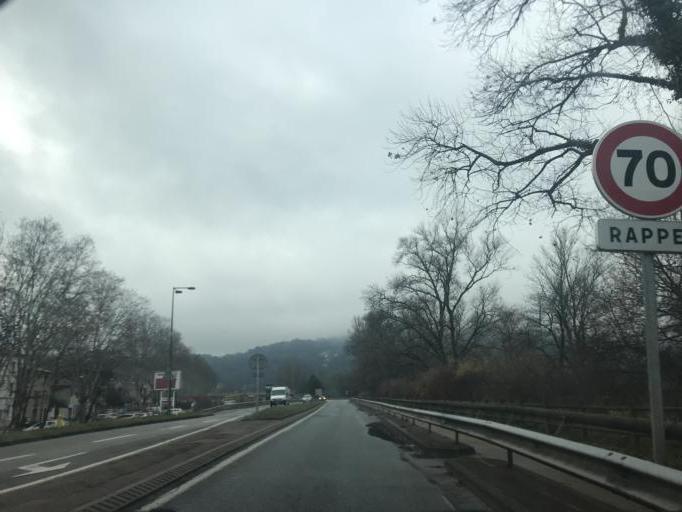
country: FR
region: Rhone-Alpes
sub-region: Departement du Rhone
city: Rochetaillee-sur-Saone
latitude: 45.8445
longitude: 4.8349
